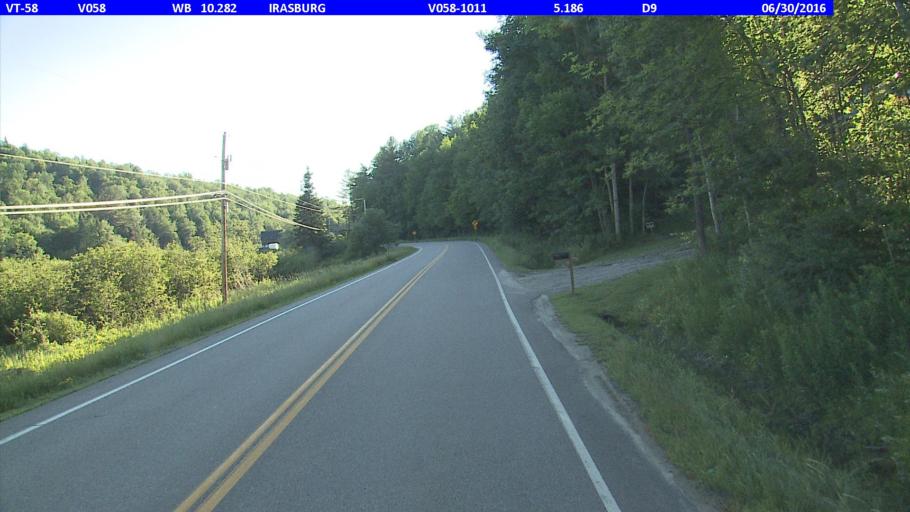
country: US
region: Vermont
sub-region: Orleans County
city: Newport
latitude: 44.8047
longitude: -72.2418
